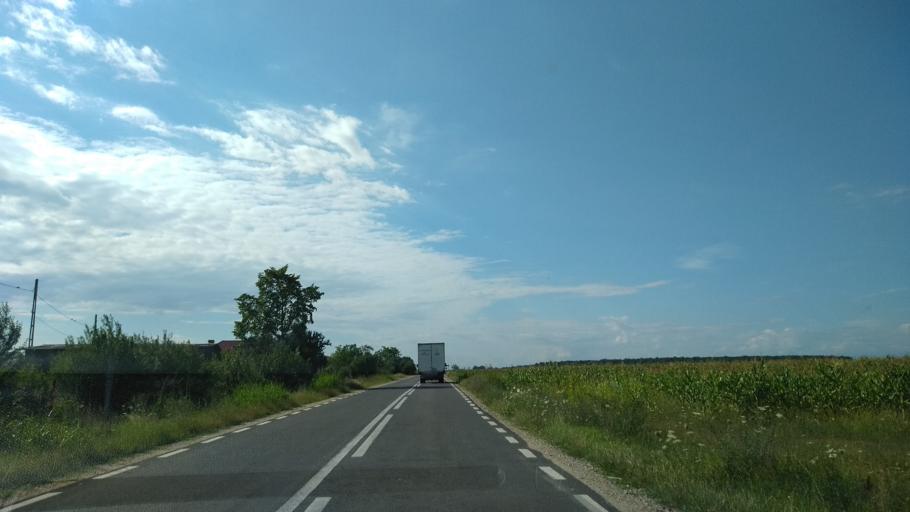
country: RO
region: Dambovita
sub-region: Comuna Uliesti
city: Uliesti
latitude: 44.6052
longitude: 25.3916
